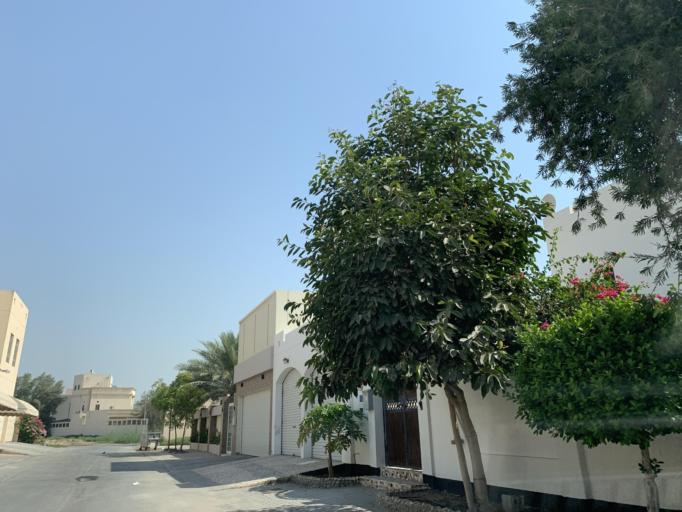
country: BH
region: Manama
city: Jidd Hafs
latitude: 26.1966
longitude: 50.5128
